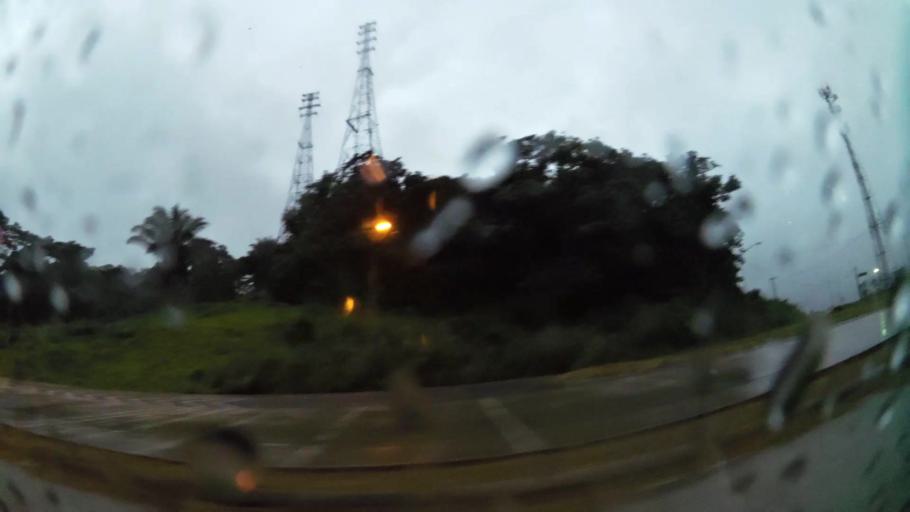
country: PA
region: Panama
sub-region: Distrito de Panama
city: Paraiso
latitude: 9.0353
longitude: -79.6302
